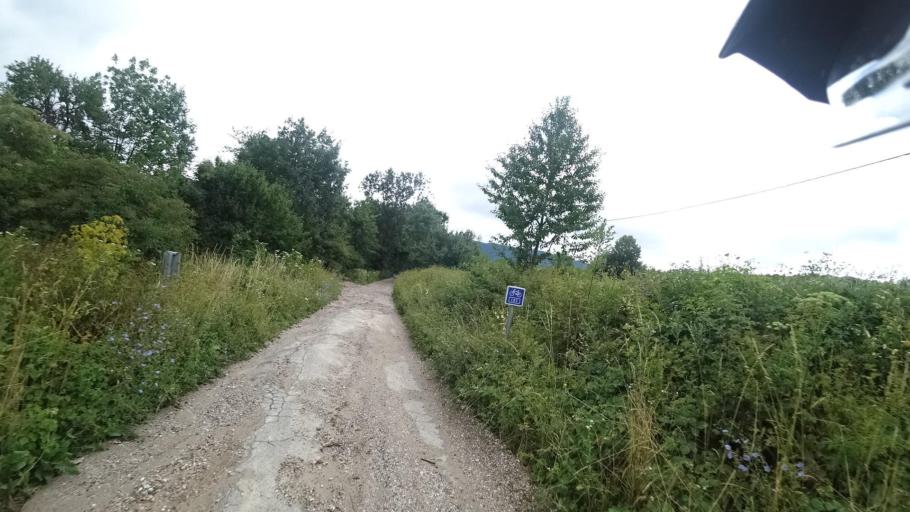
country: HR
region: Licko-Senjska
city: Otocac
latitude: 44.8608
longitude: 15.4054
